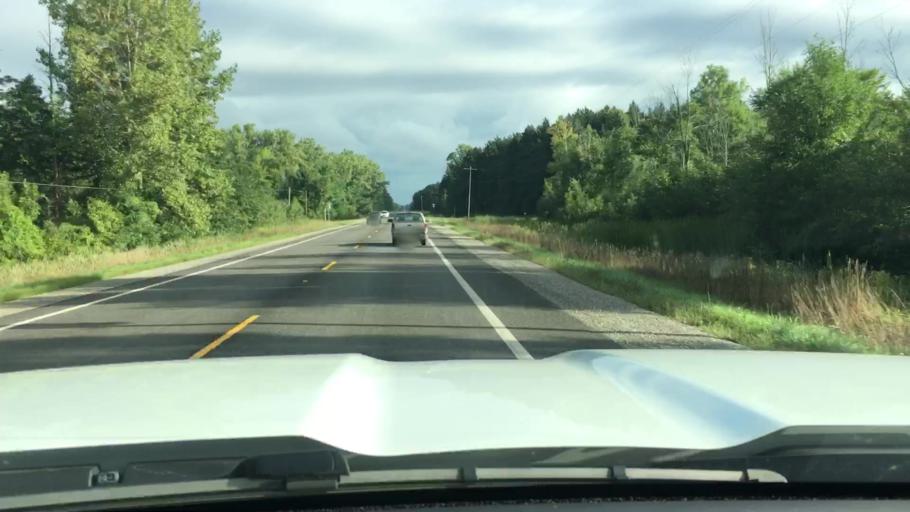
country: US
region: Michigan
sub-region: Tuscola County
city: Caro
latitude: 43.4221
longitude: -83.3844
